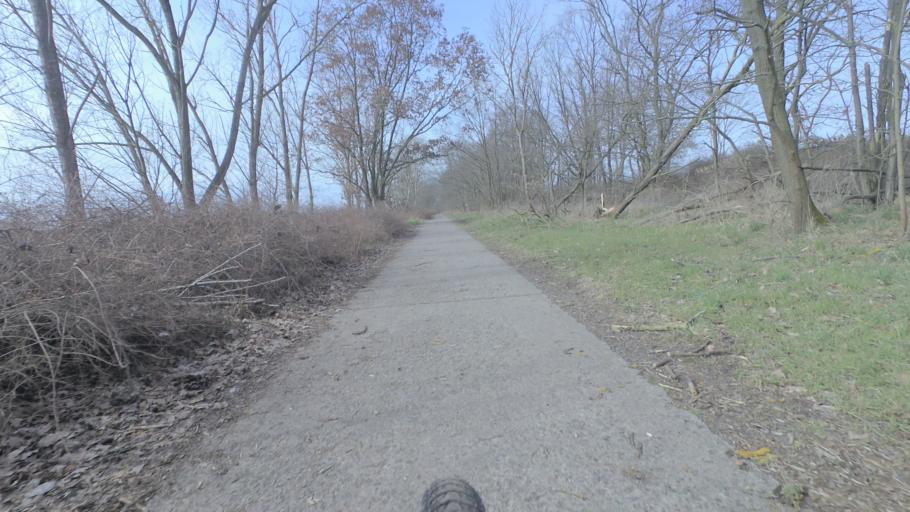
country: DE
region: Berlin
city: Marienfelde
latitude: 52.3773
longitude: 13.3624
